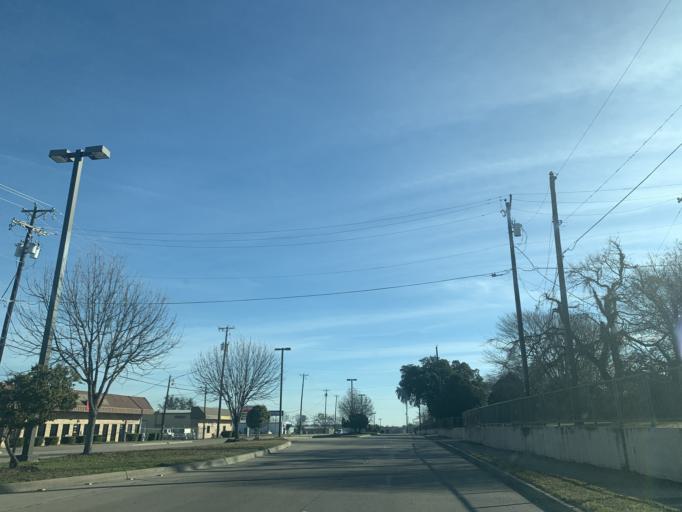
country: US
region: Texas
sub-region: Dallas County
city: DeSoto
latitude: 32.5751
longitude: -96.8272
